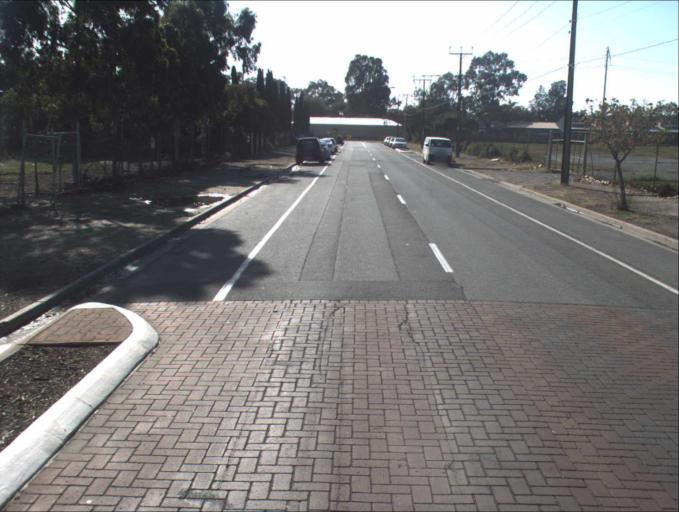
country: AU
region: South Australia
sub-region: Port Adelaide Enfield
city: Alberton
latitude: -34.8433
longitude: 138.5382
